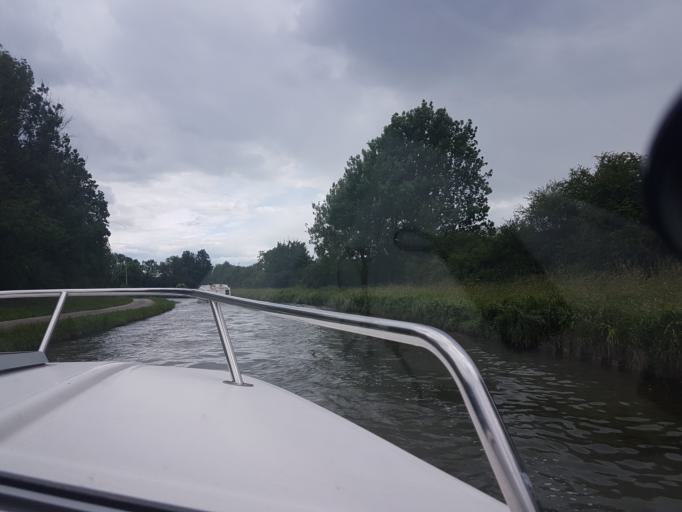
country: FR
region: Bourgogne
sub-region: Departement de l'Yonne
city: Vermenton
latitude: 47.5524
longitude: 3.6314
